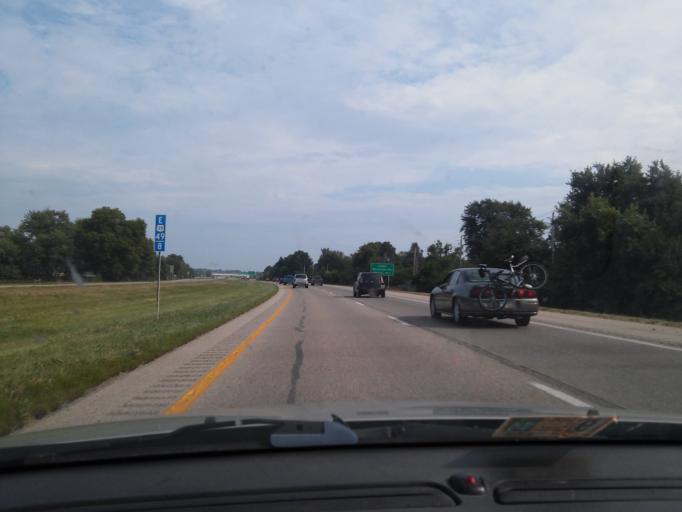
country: US
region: Ohio
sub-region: Greene County
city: Xenia
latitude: 39.6768
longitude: -83.9675
